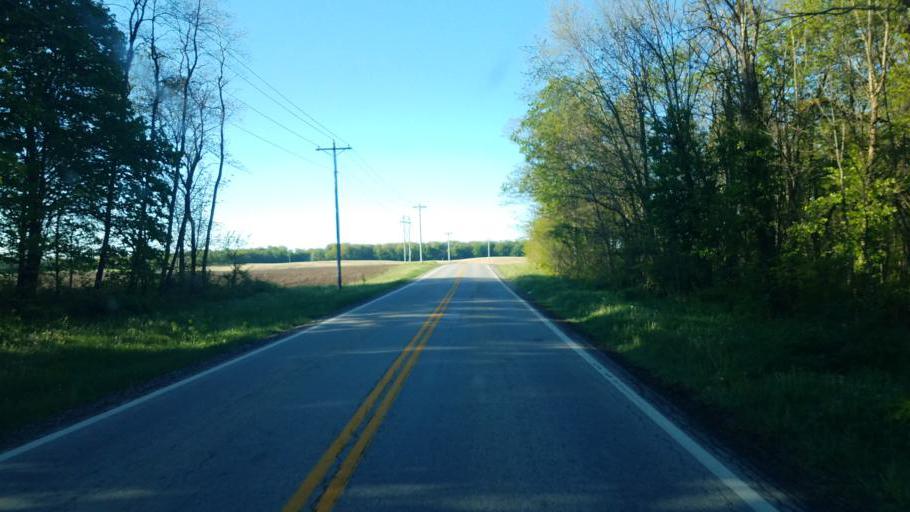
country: US
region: Ohio
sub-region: Knox County
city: Centerburg
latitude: 40.4248
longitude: -82.6993
